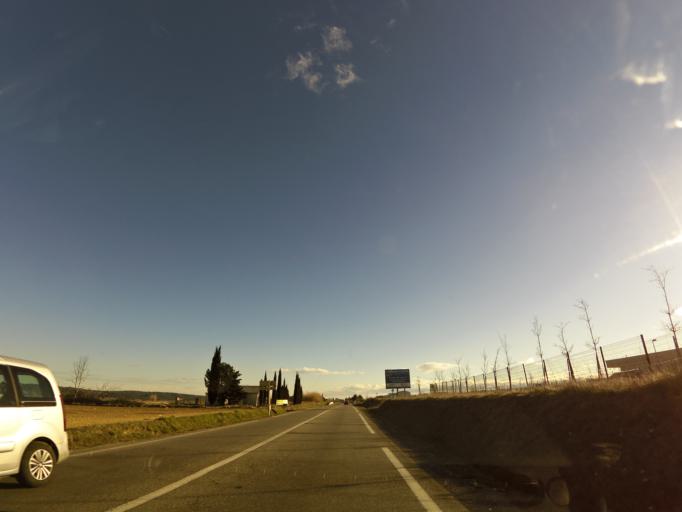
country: FR
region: Languedoc-Roussillon
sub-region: Departement du Gard
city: Calvisson
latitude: 43.7891
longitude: 4.2058
